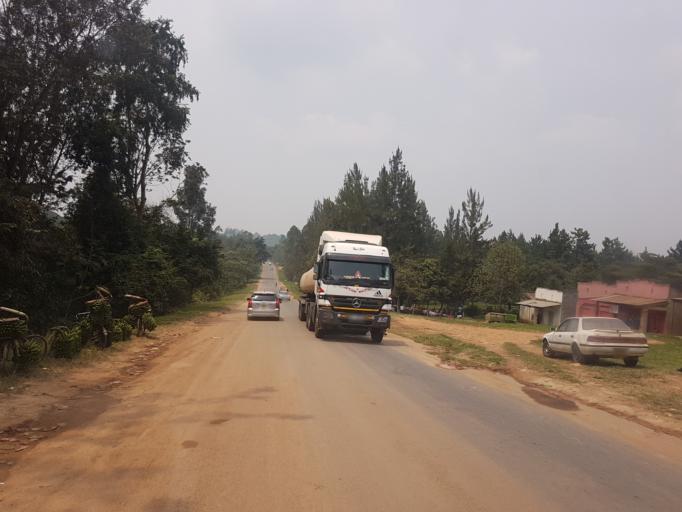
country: UG
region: Western Region
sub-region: Bushenyi District
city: Bushenyi
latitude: -0.5447
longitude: 30.2203
